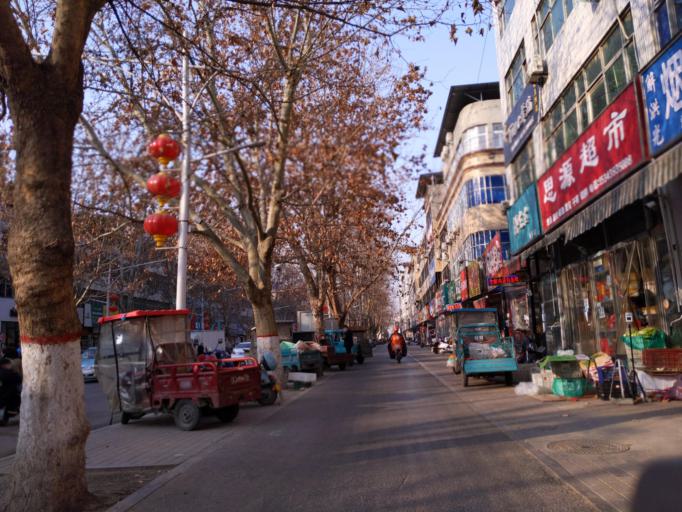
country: CN
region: Henan Sheng
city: Puyang
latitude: 35.7701
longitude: 115.0326
